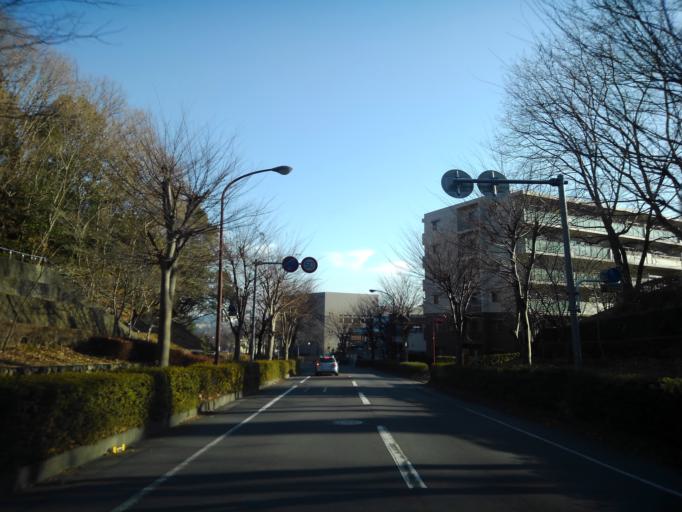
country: JP
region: Saitama
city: Hanno
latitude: 35.8440
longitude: 139.3131
